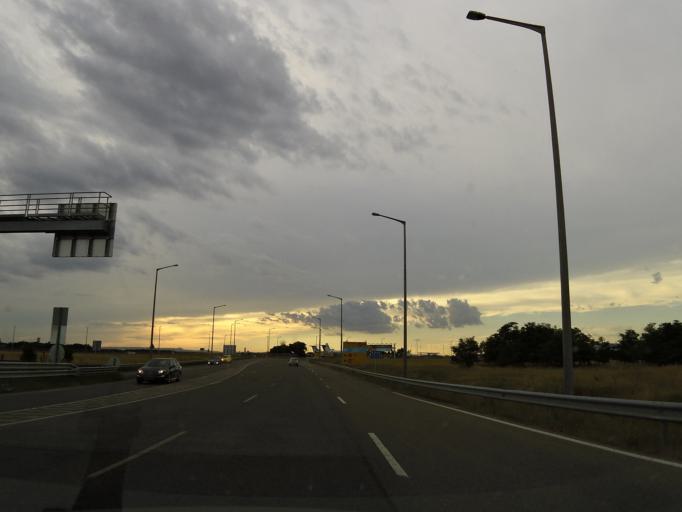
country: HU
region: Pest
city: Vecses
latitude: 47.4245
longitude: 19.2648
